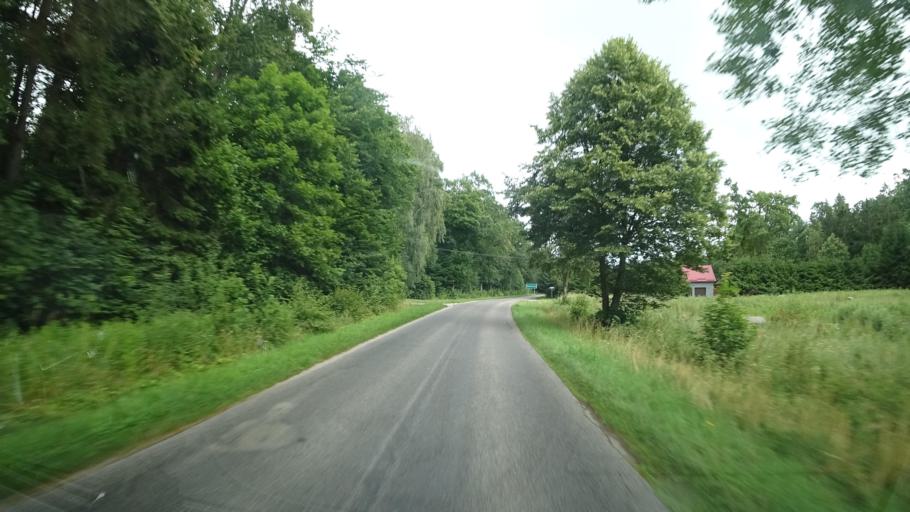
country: PL
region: Warmian-Masurian Voivodeship
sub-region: Powiat goldapski
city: Goldap
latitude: 54.3089
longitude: 22.4068
